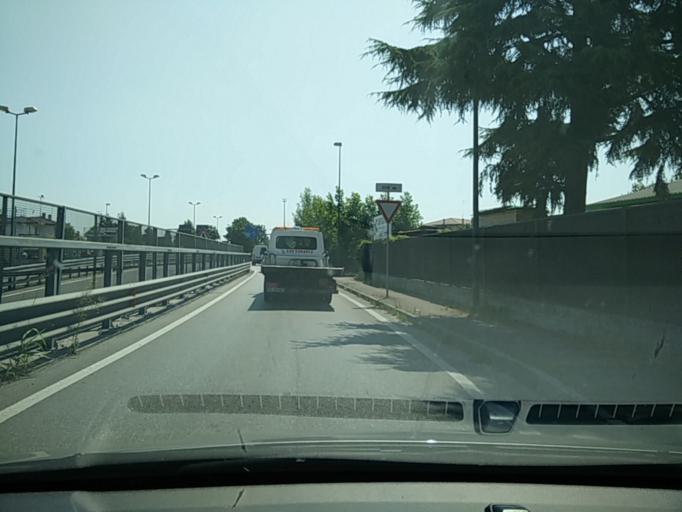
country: IT
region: Veneto
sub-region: Provincia di Venezia
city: Zelarino
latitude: 45.5155
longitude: 12.2395
